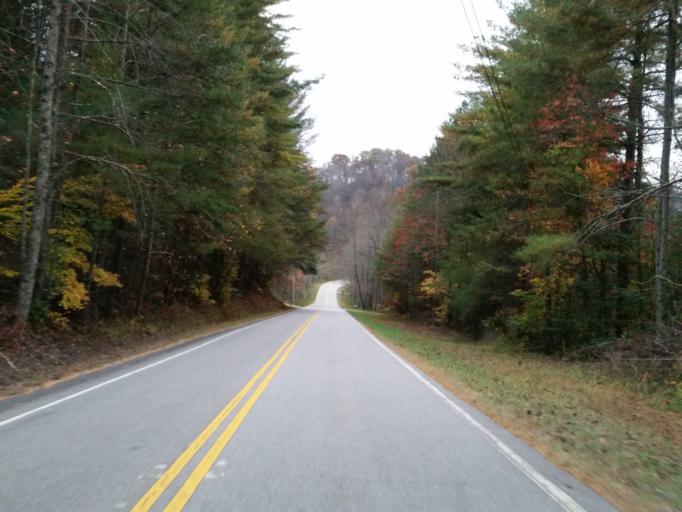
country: US
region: Georgia
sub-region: Union County
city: Blairsville
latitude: 34.7336
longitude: -84.0808
